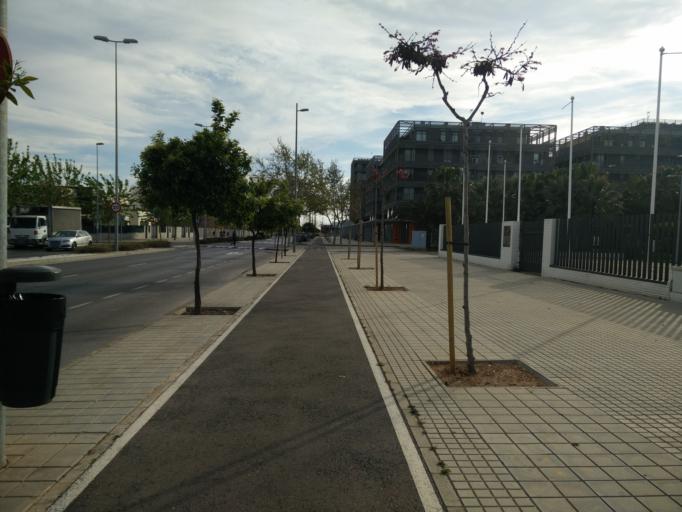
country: ES
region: Valencia
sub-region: Provincia de Castello
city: Castello de la Plana
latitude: 39.9781
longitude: -0.0563
